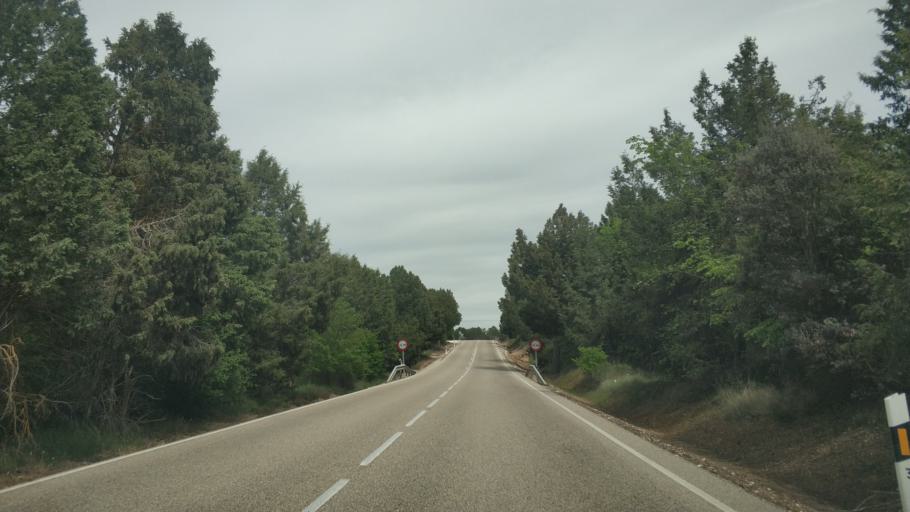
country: ES
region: Castille and Leon
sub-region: Provincia de Soria
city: Valdenebro
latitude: 41.5643
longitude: -2.9886
